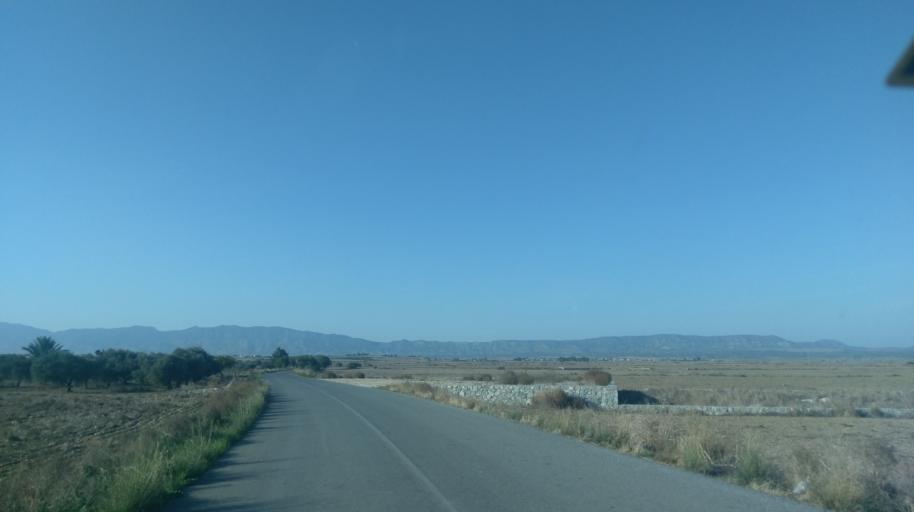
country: CY
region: Ammochostos
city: Lefkonoiko
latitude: 35.2234
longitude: 33.6964
